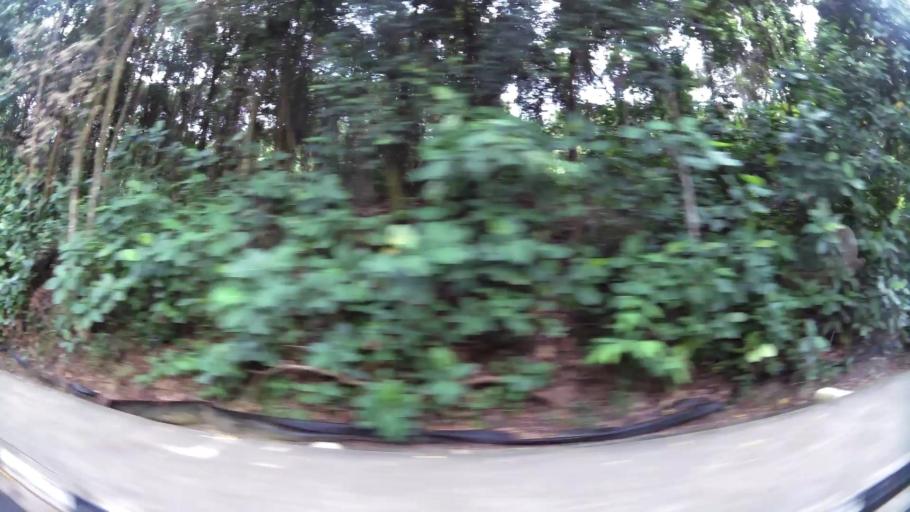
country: SG
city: Singapore
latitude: 1.2885
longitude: 103.7844
